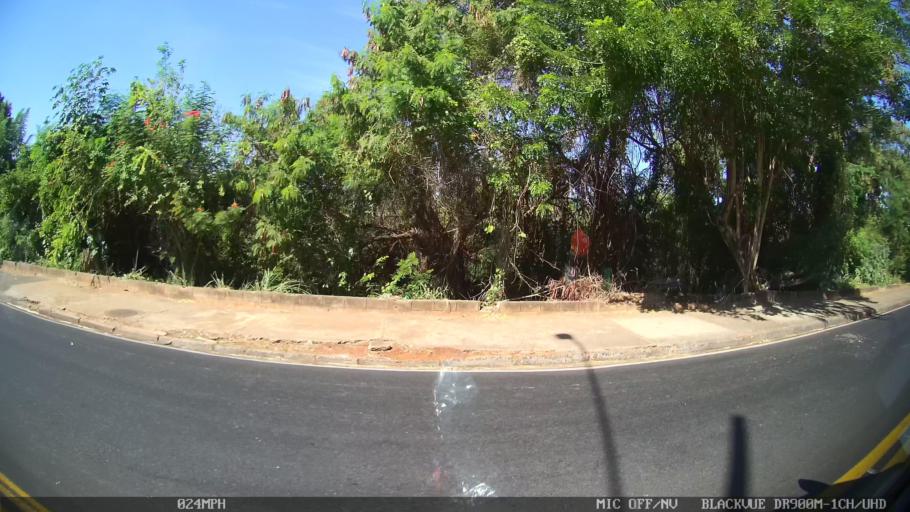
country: BR
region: Sao Paulo
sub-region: Sao Jose Do Rio Preto
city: Sao Jose do Rio Preto
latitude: -20.8039
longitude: -49.4198
